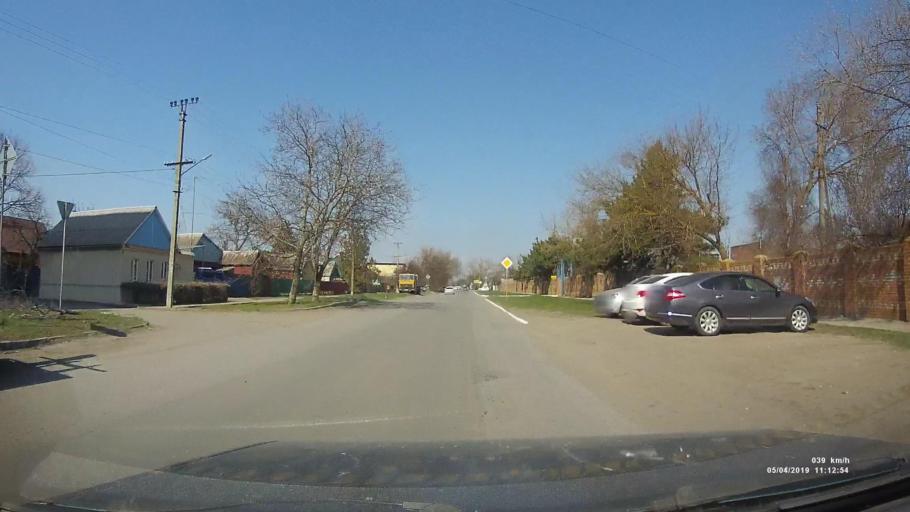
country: RU
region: Rostov
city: Azov
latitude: 47.1000
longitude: 39.4345
